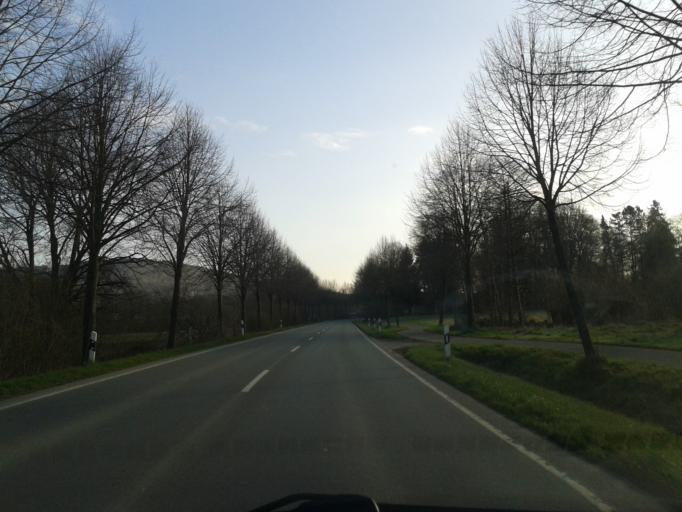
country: DE
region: North Rhine-Westphalia
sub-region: Regierungsbezirk Detmold
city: Blomberg
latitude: 51.9183
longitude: 9.1458
